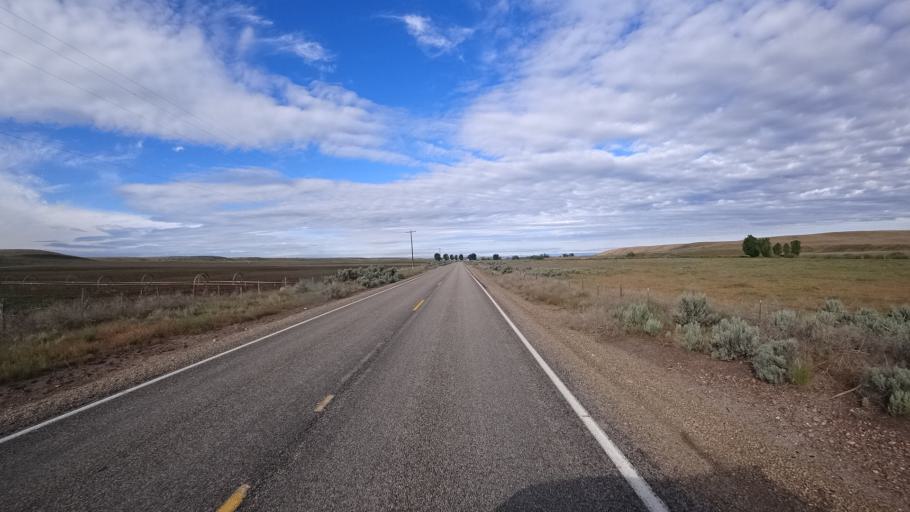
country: US
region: Idaho
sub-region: Ada County
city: Star
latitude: 43.7636
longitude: -116.5040
